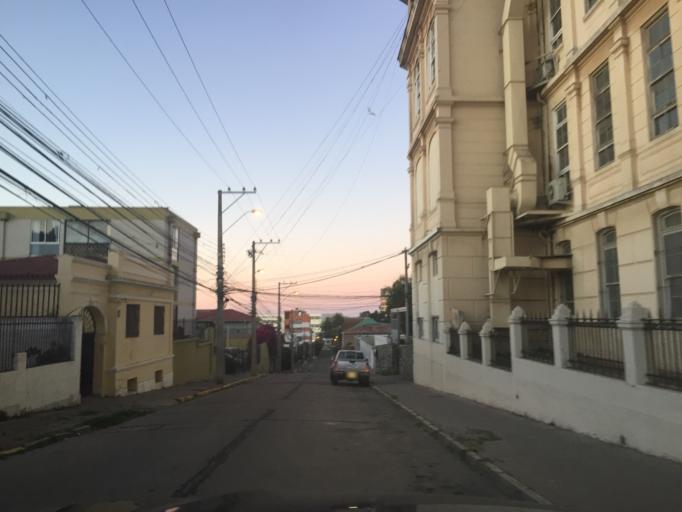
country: CL
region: Valparaiso
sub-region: Provincia de Valparaiso
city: Valparaiso
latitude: -33.0255
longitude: -71.6371
